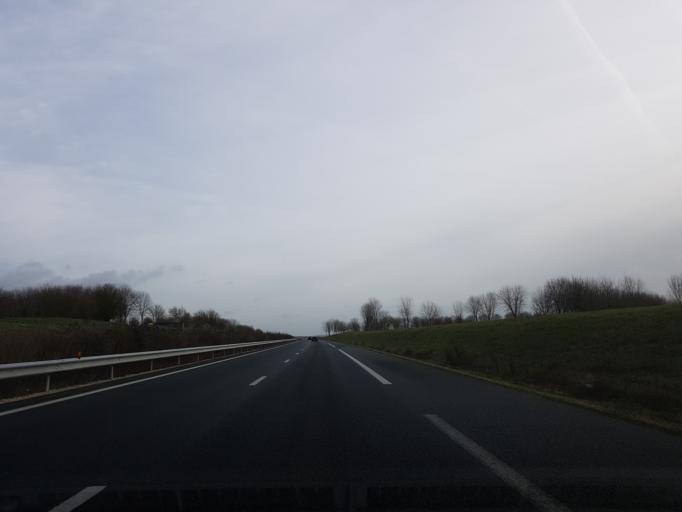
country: FR
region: Bourgogne
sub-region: Departement de l'Yonne
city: Thorigny-sur-Oreuse
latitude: 48.2456
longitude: 3.5505
